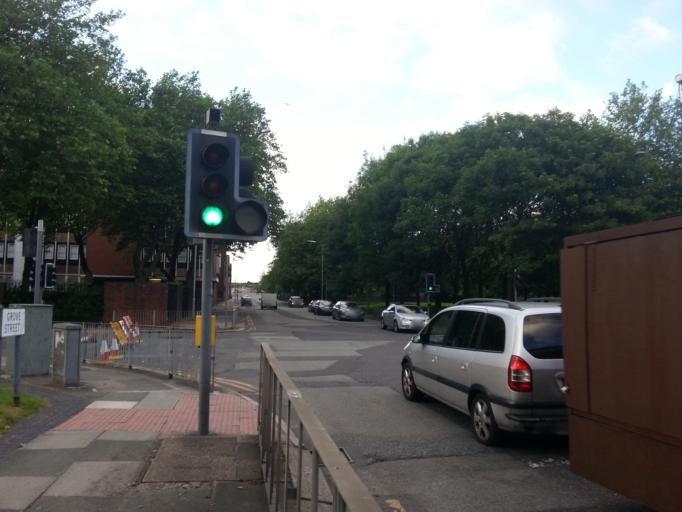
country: GB
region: England
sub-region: Liverpool
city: Liverpool
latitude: 53.4030
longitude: -2.9621
